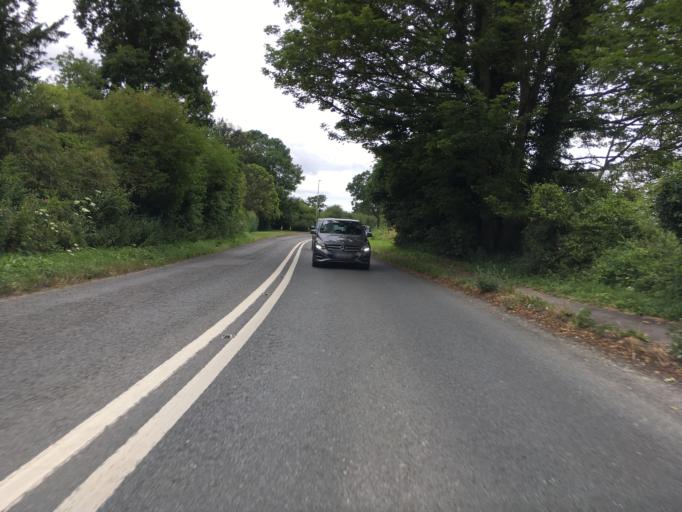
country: GB
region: England
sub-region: Gloucestershire
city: Charlton Kings
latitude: 51.8791
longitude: -2.0324
